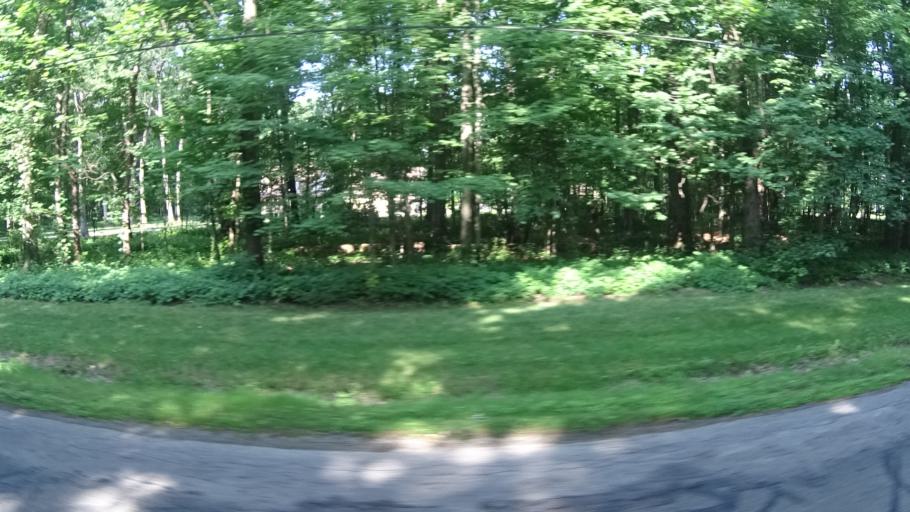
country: US
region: Ohio
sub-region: Lorain County
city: Vermilion
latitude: 41.3685
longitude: -82.4304
